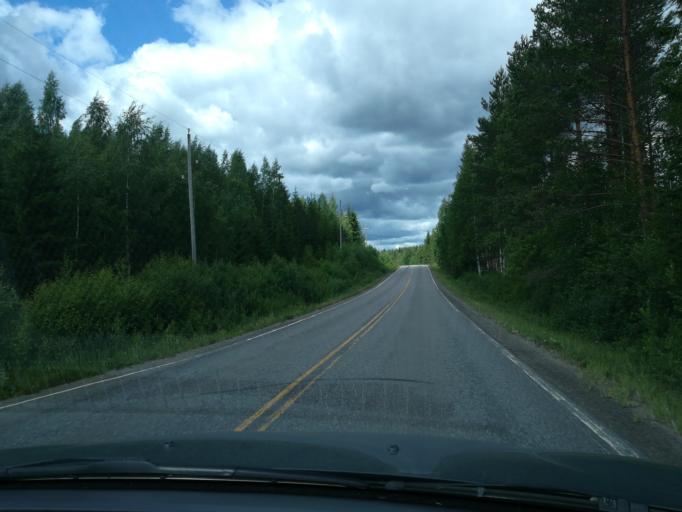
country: FI
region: Southern Savonia
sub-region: Mikkeli
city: Maentyharju
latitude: 61.3623
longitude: 27.0603
